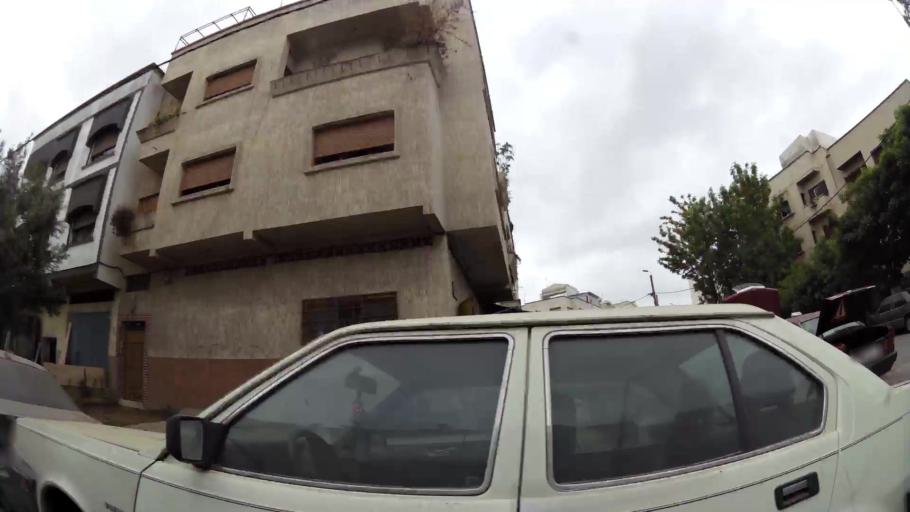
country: MA
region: Rabat-Sale-Zemmour-Zaer
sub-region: Rabat
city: Rabat
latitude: 33.9834
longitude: -6.8130
